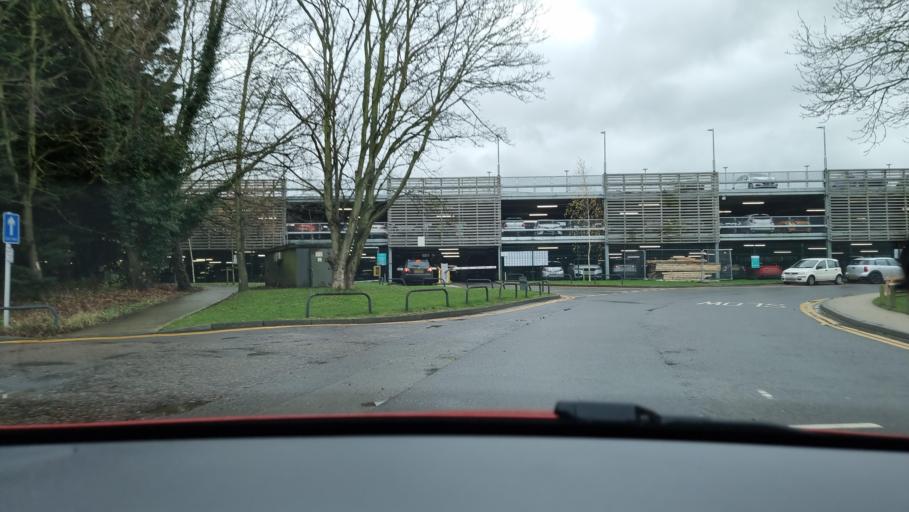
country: GB
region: England
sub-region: Buckinghamshire
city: Aylesbury
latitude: 51.7979
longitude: -0.7993
